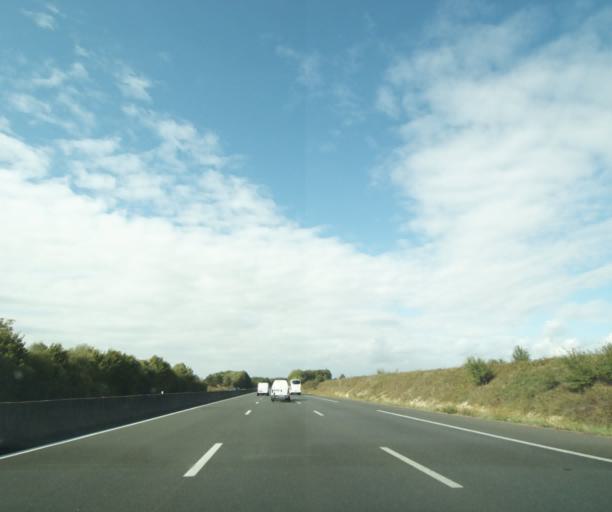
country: FR
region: Centre
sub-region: Departement d'Eure-et-Loir
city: Baigneaux
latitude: 48.1591
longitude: 1.8547
